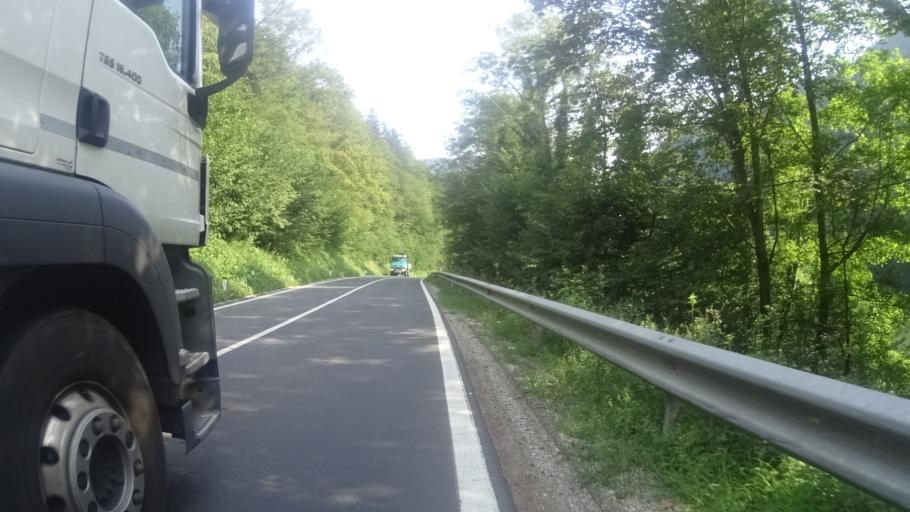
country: SI
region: Lovrenc na Pohorju
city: Lovrenc na Pohorju
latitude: 46.5686
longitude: 15.4392
